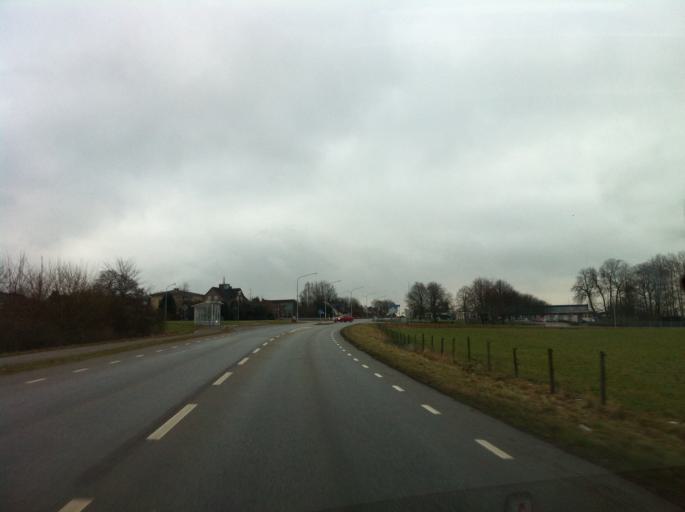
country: SE
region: Skane
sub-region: Helsingborg
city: Glumslov
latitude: 55.9452
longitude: 12.8062
